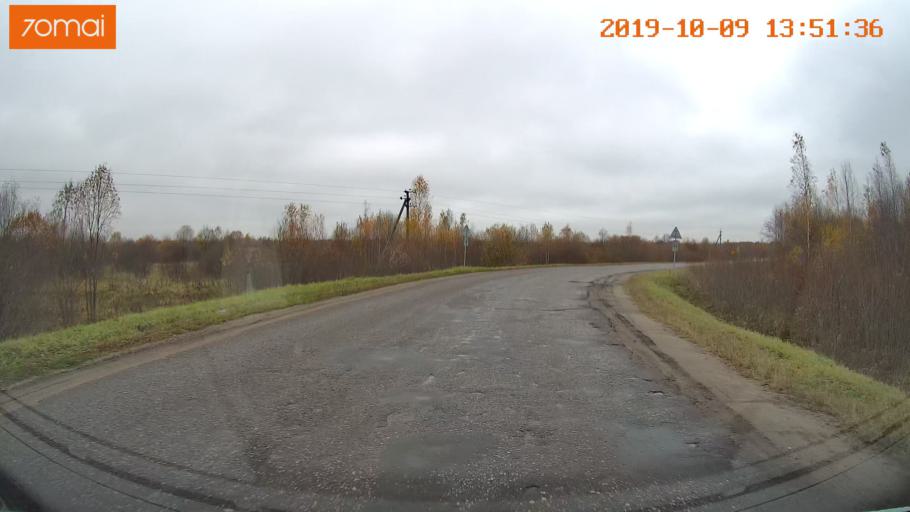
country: RU
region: Kostroma
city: Buy
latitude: 58.4083
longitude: 41.2404
